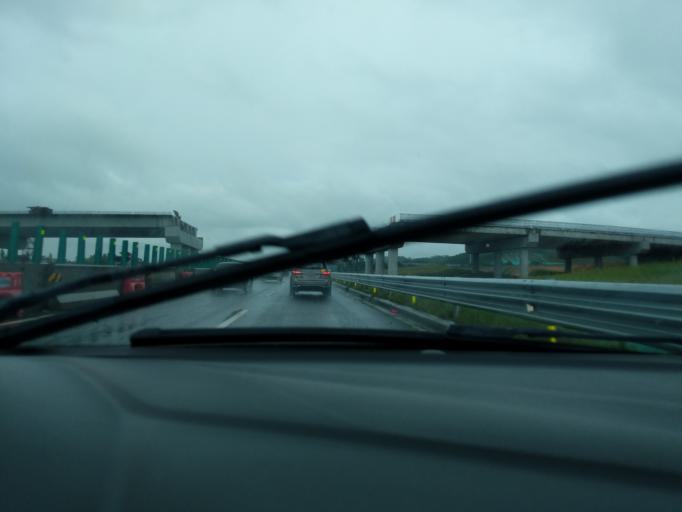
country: CN
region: Guangdong
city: Yueshan
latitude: 22.4641
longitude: 112.7097
